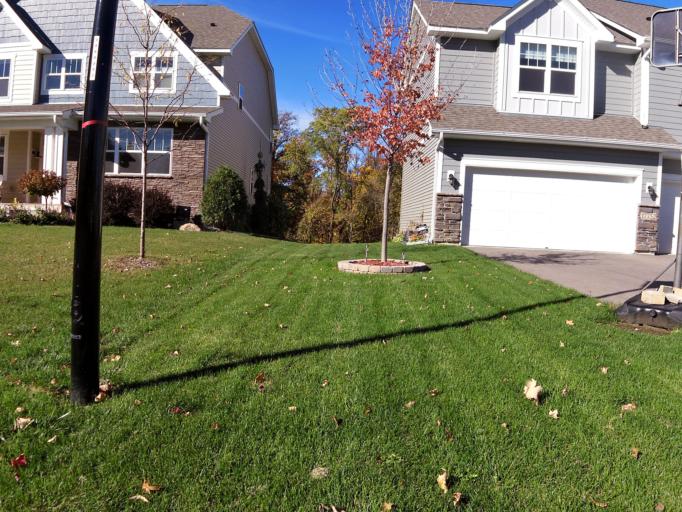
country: US
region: Minnesota
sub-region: Scott County
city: Prior Lake
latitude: 44.6924
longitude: -93.4495
